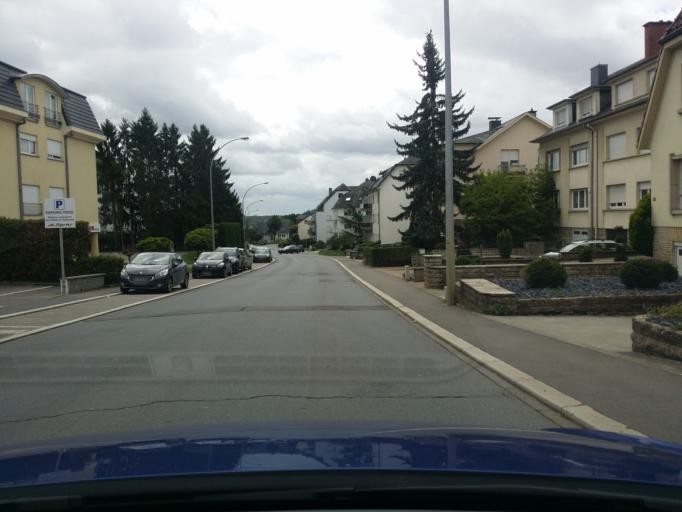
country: LU
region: Luxembourg
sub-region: Canton de Luxembourg
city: Strassen
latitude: 49.6210
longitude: 6.0645
